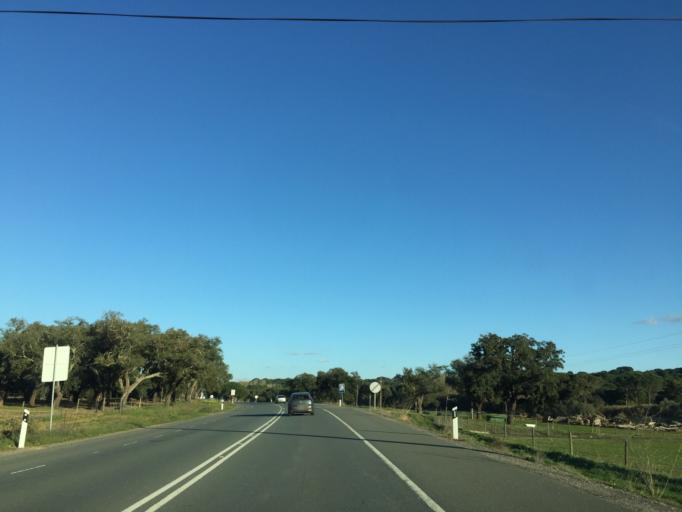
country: PT
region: Setubal
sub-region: Grandola
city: Grandola
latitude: 38.1213
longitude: -8.4428
